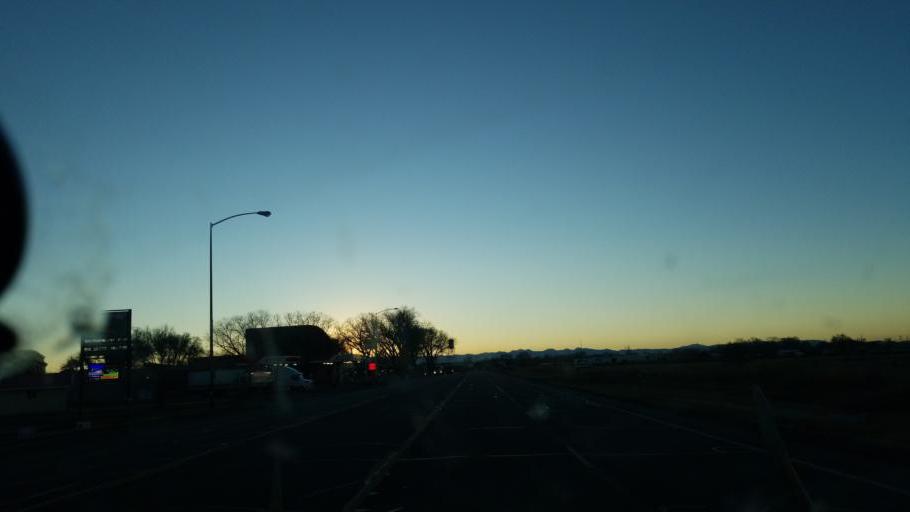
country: US
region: Colorado
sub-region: Alamosa County
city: Alamosa
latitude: 37.4699
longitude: -105.8826
